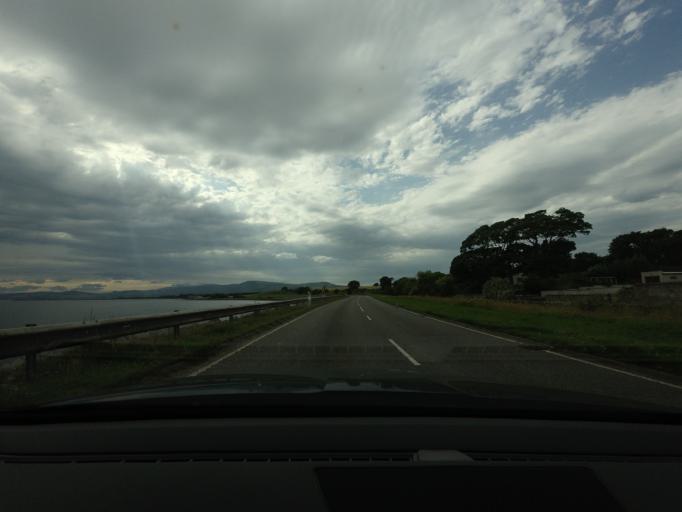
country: GB
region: Scotland
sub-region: Highland
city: Invergordon
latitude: 57.6920
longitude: -4.1992
